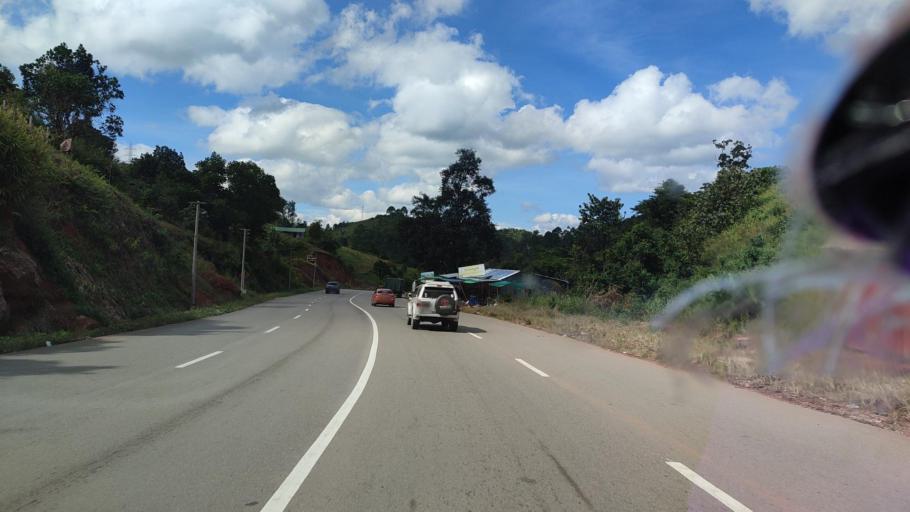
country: MM
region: Mandalay
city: Yamethin
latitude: 20.6563
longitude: 96.5438
